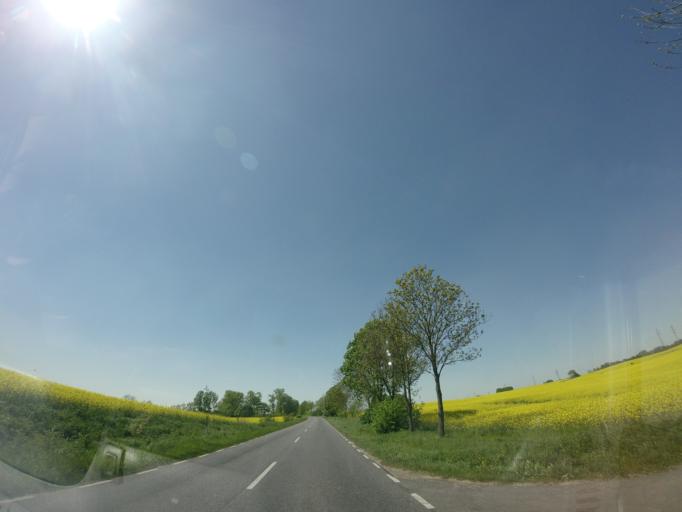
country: PL
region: West Pomeranian Voivodeship
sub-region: Powiat mysliborski
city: Barlinek
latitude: 52.9939
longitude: 15.1611
